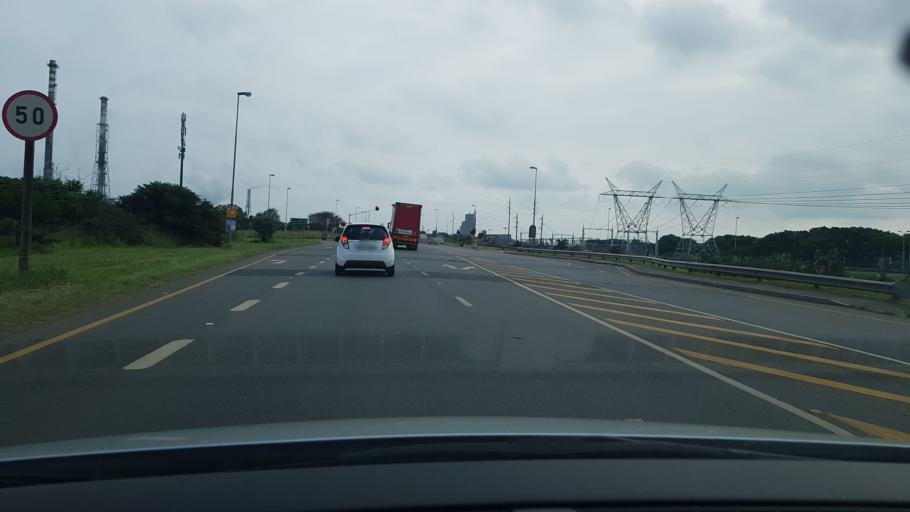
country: ZA
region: KwaZulu-Natal
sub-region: uThungulu District Municipality
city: Richards Bay
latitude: -28.7672
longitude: 32.0363
